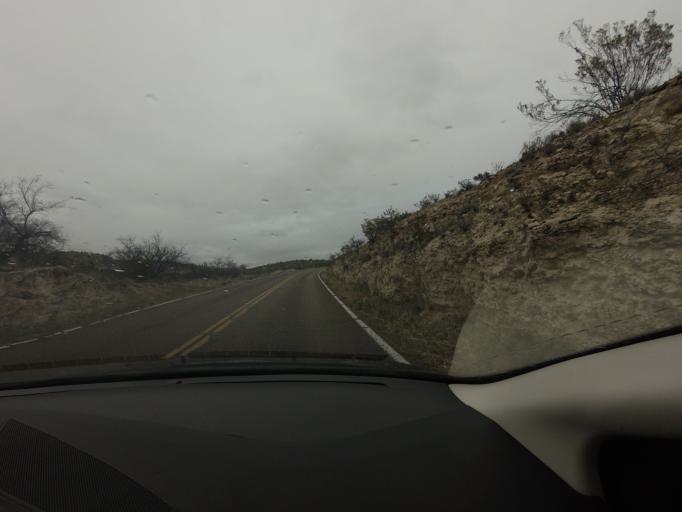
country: US
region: Arizona
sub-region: Yavapai County
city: Camp Verde
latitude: 34.6114
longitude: -111.8504
